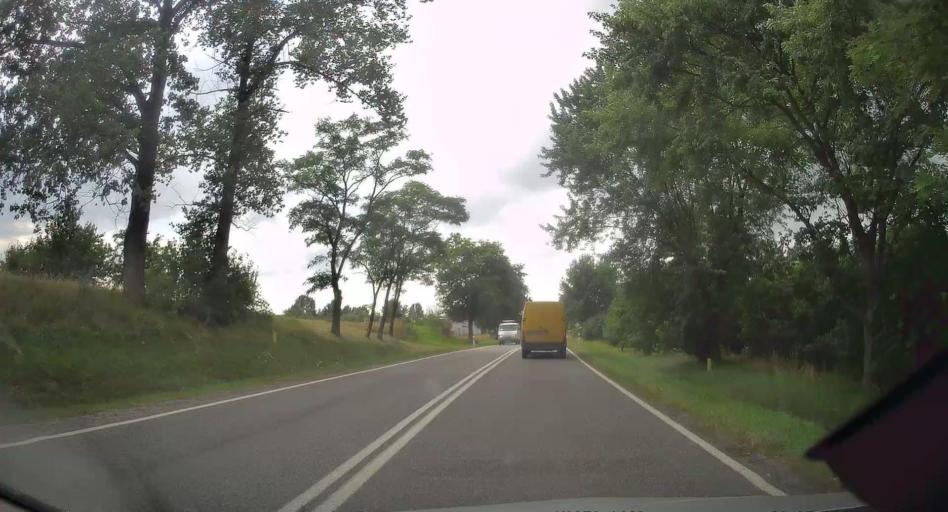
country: PL
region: Lodz Voivodeship
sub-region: Powiat skierniewicki
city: Gluchow
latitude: 51.7713
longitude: 20.1471
